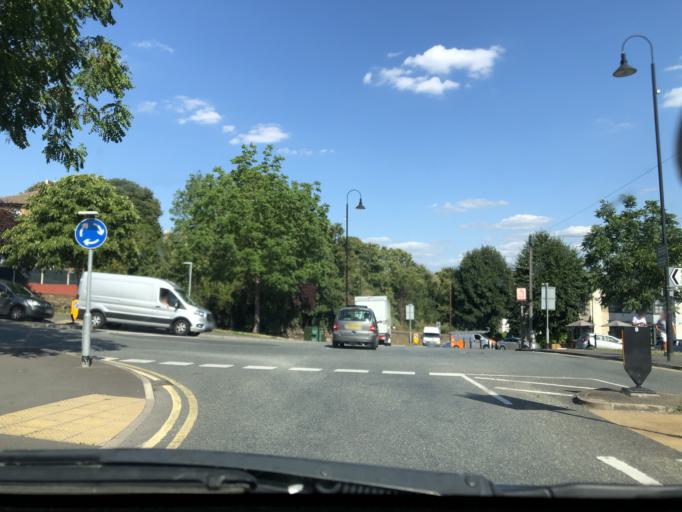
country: GB
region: England
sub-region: Greater London
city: Bexley
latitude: 51.4541
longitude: 0.1746
